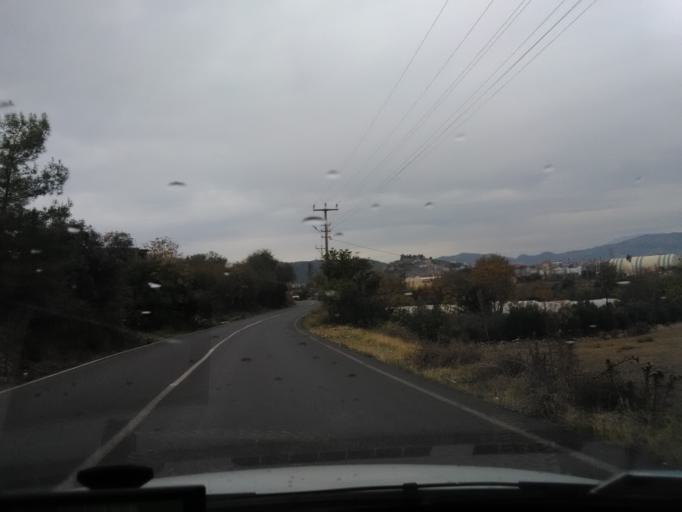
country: TR
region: Antalya
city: Gazipasa
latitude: 36.2589
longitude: 32.3182
